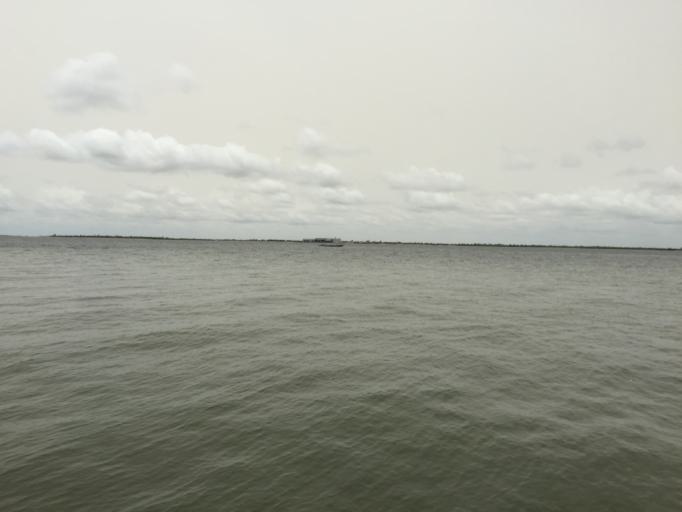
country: SN
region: Fatick
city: Foundiougne
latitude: 14.1299
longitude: -16.4687
